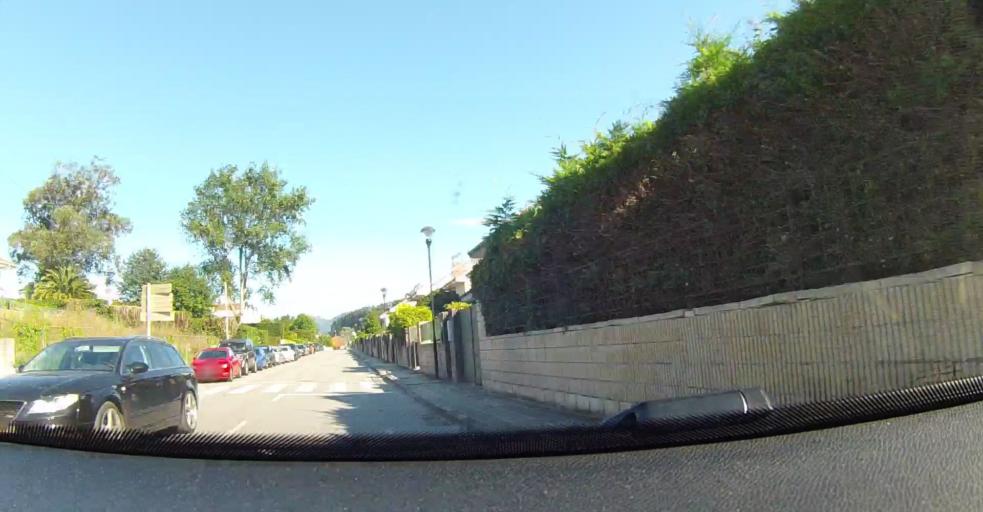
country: ES
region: Asturias
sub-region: Province of Asturias
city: Ribadesella
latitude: 43.4667
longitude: -5.0775
